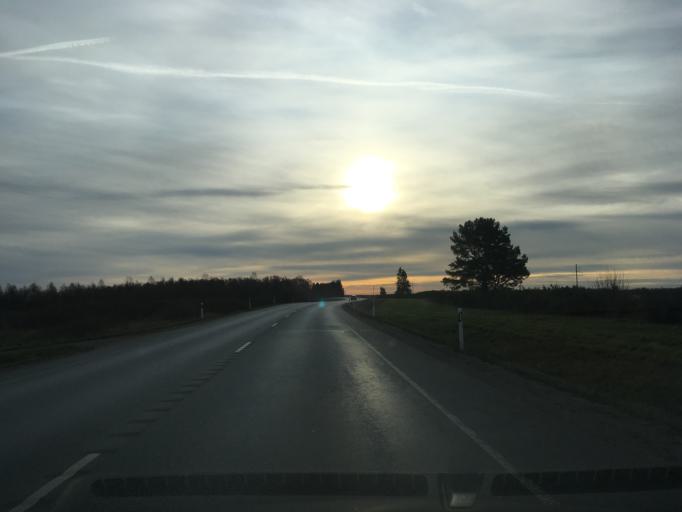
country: EE
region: Ida-Virumaa
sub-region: Kivioli linn
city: Kivioli
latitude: 59.4208
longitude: 26.9700
